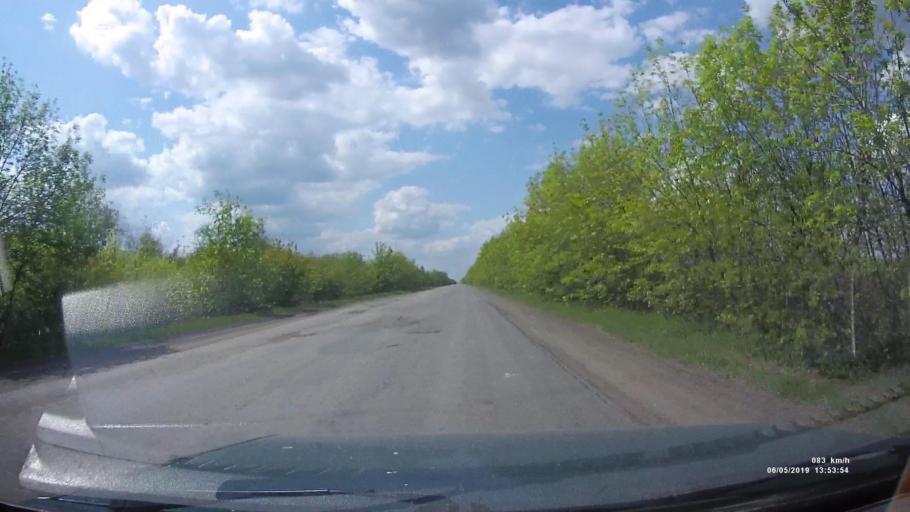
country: RU
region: Rostov
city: Melikhovskaya
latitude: 47.6712
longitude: 40.4553
